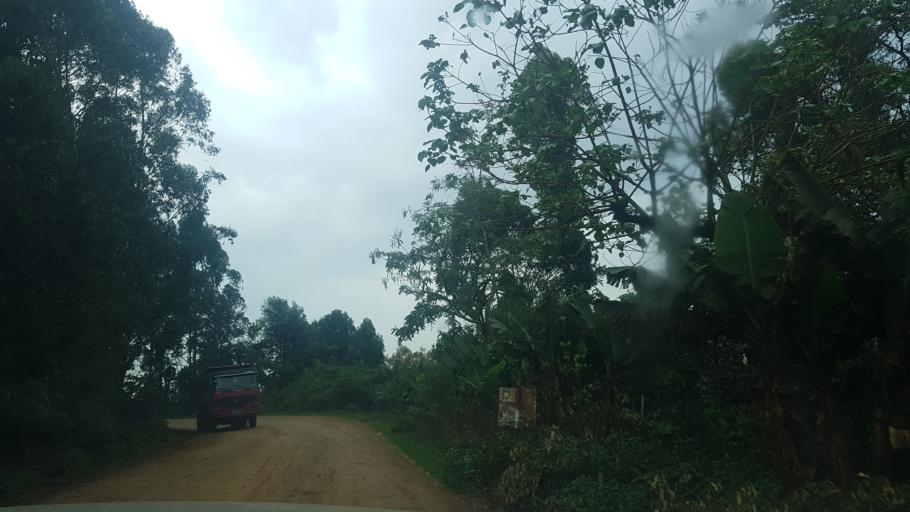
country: ET
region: Oromiya
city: Gore
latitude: 7.8921
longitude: 35.4889
